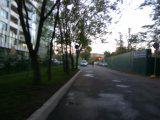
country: RU
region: Moscow
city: Pokrovskoye-Streshnevo
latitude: 55.8135
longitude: 37.4808
